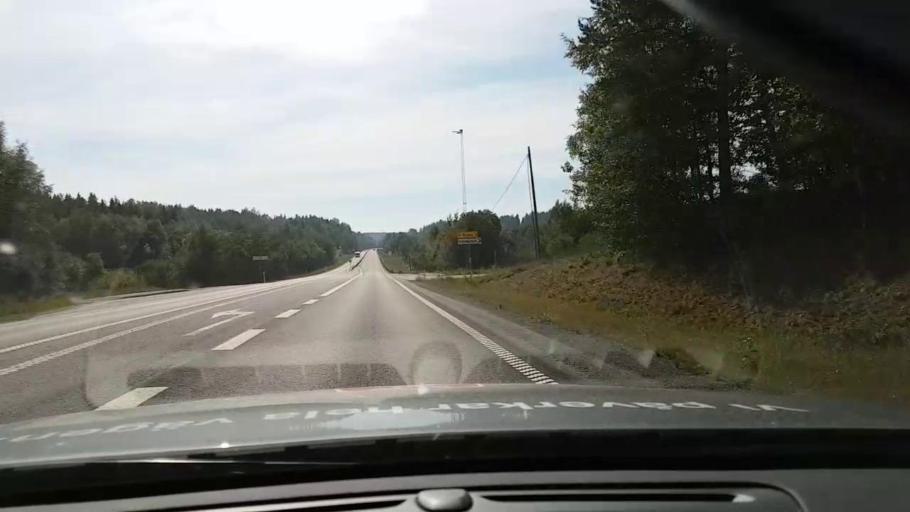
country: SE
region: Vaesternorrland
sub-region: OErnskoeldsviks Kommun
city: Husum
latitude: 63.3629
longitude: 19.1788
